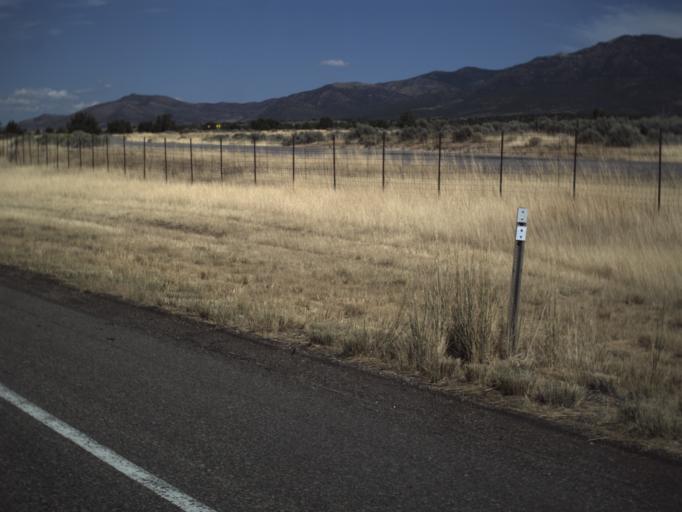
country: US
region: Utah
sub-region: Millard County
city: Fillmore
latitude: 39.0789
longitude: -112.2783
